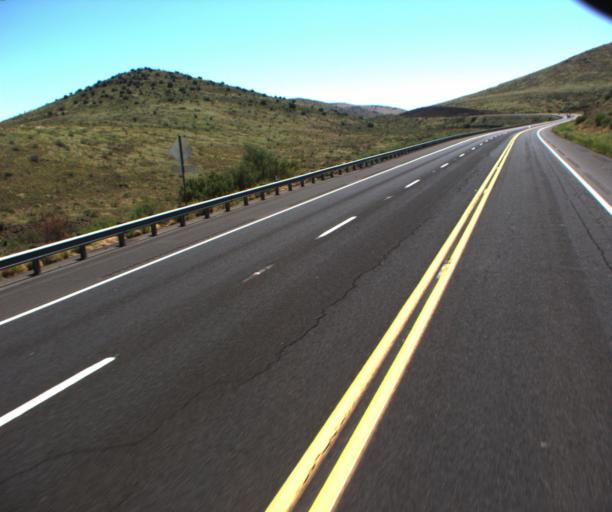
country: US
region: Arizona
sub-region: Greenlee County
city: Clifton
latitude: 32.9006
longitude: -109.2670
